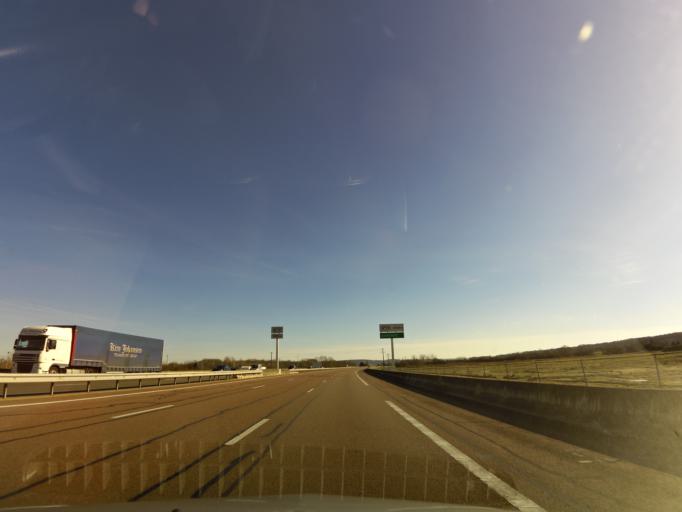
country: FR
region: Bourgogne
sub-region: Departement de l'Yonne
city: Appoigny
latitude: 47.8625
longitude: 3.5310
